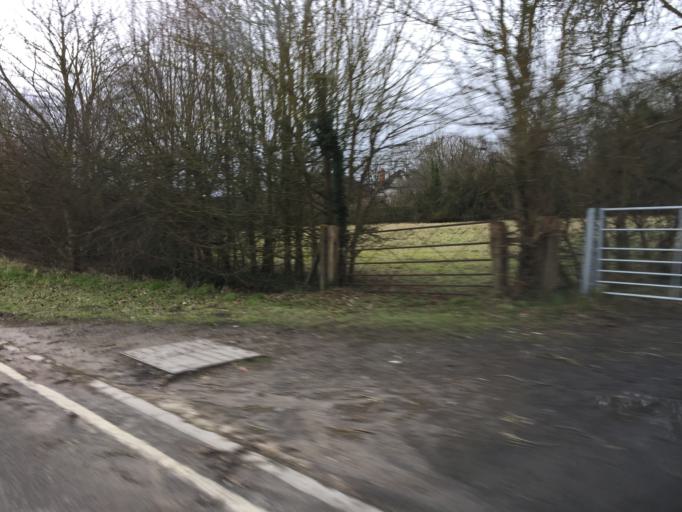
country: GB
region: England
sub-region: Oxfordshire
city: Harwell
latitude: 51.5796
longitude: -1.2649
